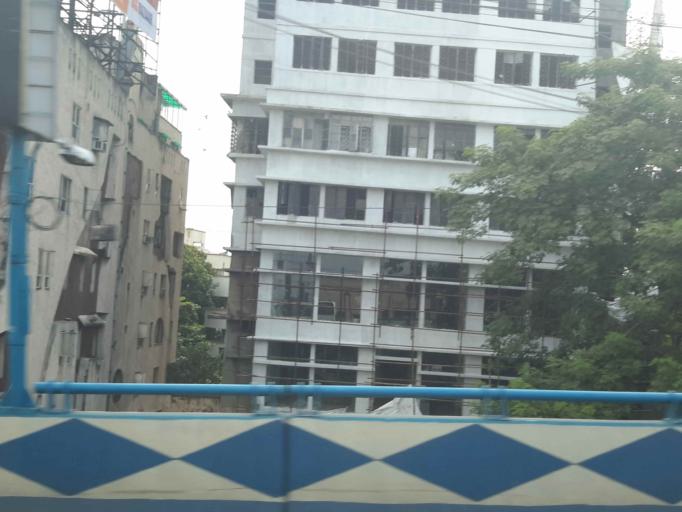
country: IN
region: West Bengal
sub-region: Kolkata
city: Kolkata
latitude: 22.5191
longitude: 88.3655
